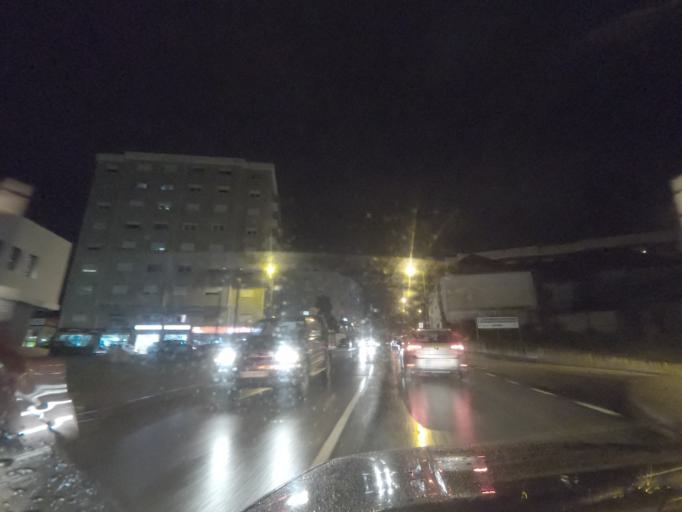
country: PT
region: Vila Real
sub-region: Vila Real
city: Vila Real
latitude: 41.3005
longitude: -7.7492
